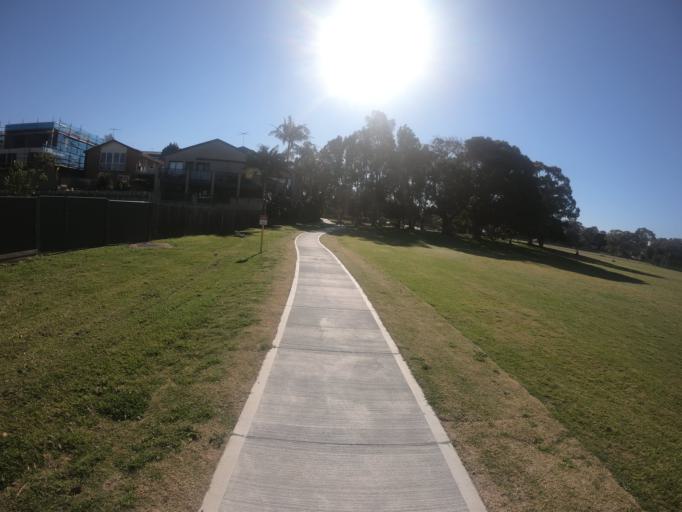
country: AU
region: New South Wales
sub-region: Canada Bay
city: Concord
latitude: -33.8288
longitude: 151.1110
